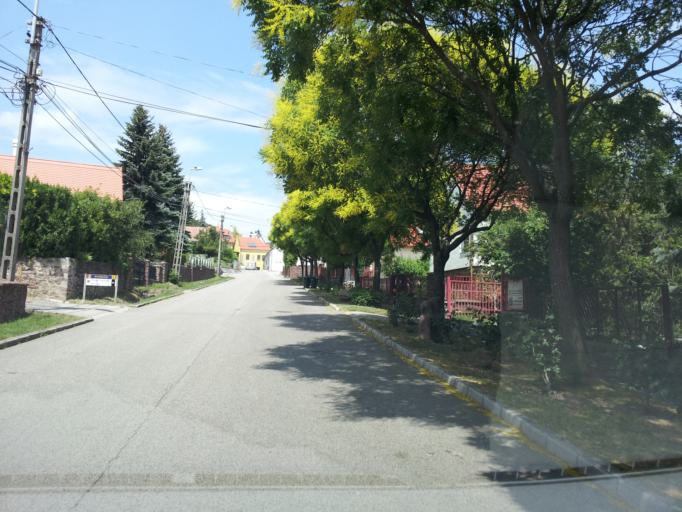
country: HU
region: Veszprem
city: Csopak
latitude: 46.9933
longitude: 17.9745
